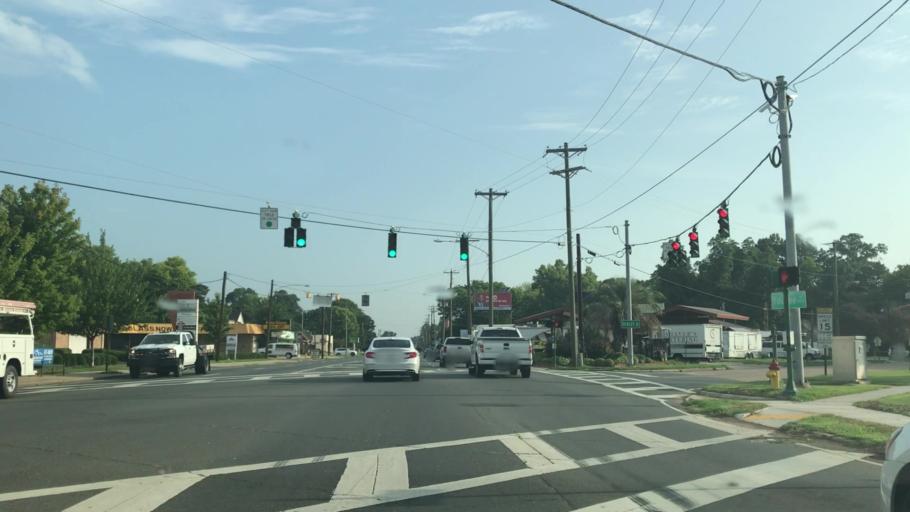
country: US
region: Louisiana
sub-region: Bossier Parish
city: Bossier City
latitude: 32.4670
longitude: -93.7221
